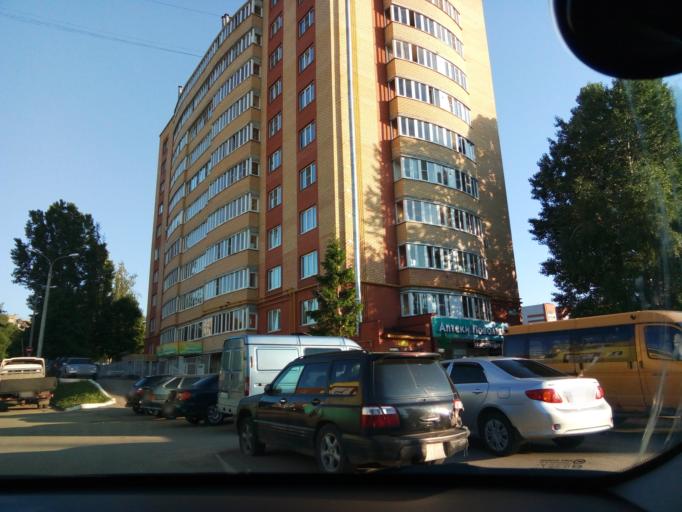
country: RU
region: Chuvashia
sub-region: Cheboksarskiy Rayon
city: Cheboksary
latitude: 56.1084
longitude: 47.2996
